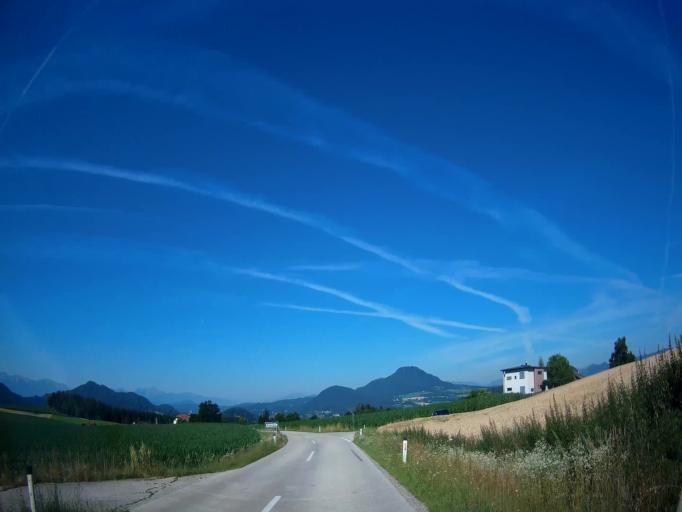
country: AT
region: Carinthia
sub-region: Politischer Bezirk Klagenfurt Land
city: Maria Saal
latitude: 46.6964
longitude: 14.3907
